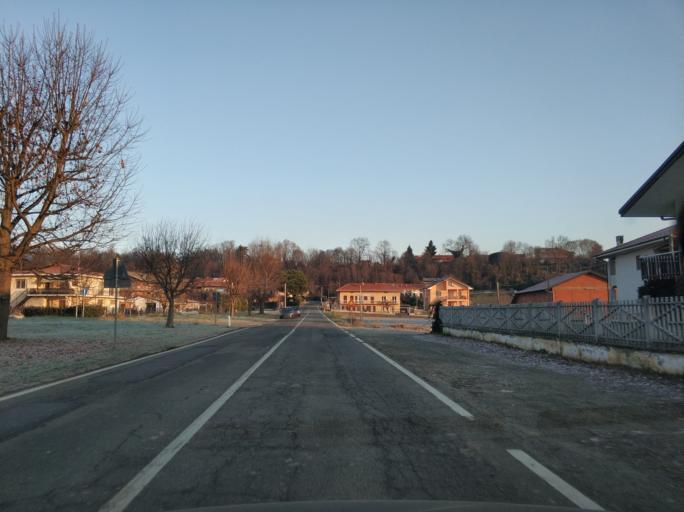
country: IT
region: Piedmont
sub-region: Provincia di Torino
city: Nole
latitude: 45.2537
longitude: 7.5759
